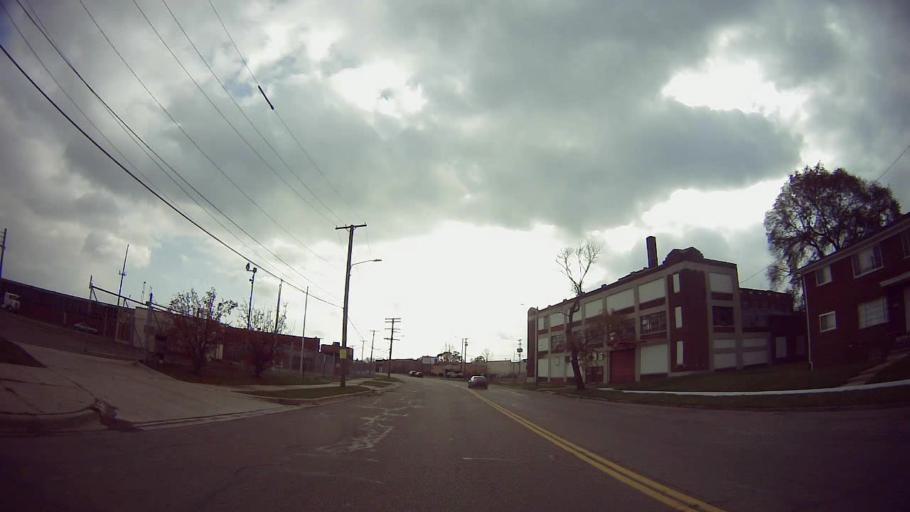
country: US
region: Michigan
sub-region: Wayne County
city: Highland Park
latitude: 42.3982
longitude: -83.1353
